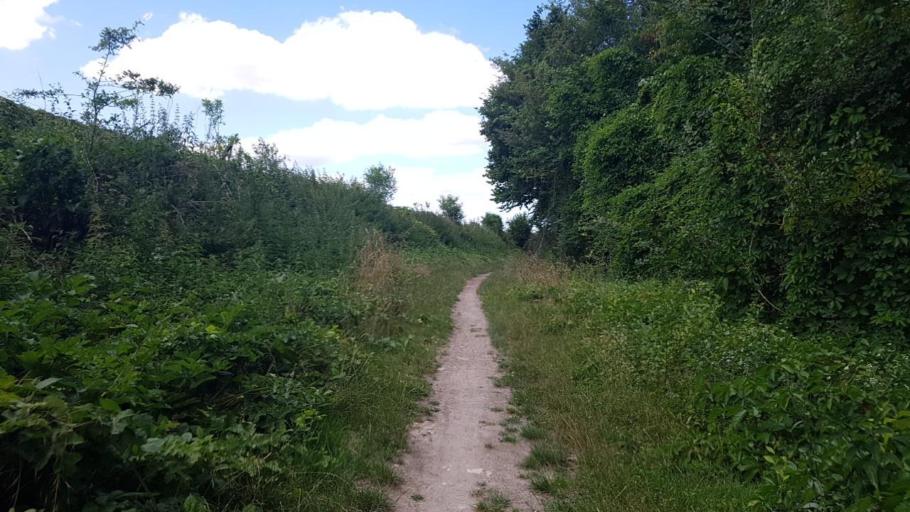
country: FR
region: Ile-de-France
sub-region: Departement de Seine-et-Marne
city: Claye-Souilly
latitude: 48.9707
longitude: 2.6709
